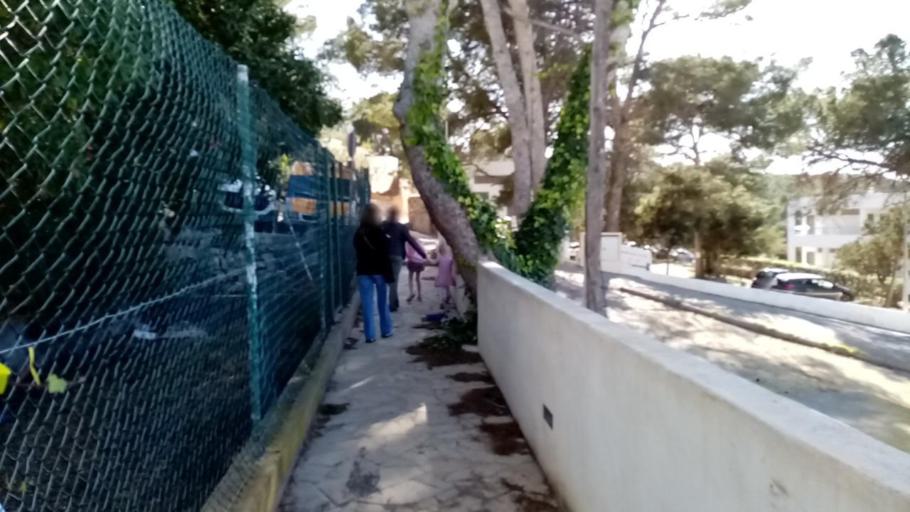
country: ES
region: Balearic Islands
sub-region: Illes Balears
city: Sant Joan de Labritja
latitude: 39.1091
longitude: 1.5172
